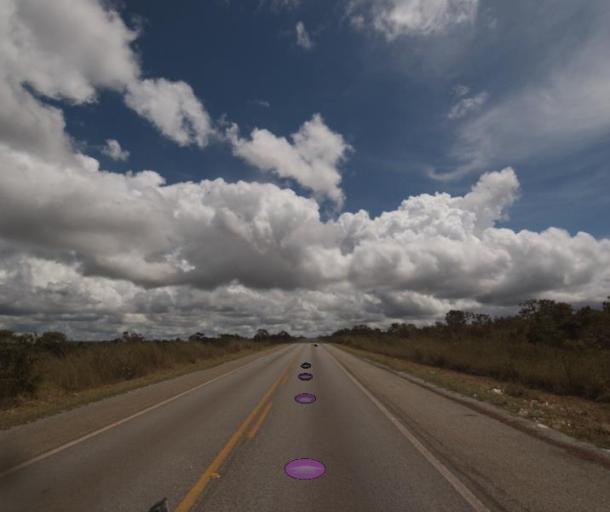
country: BR
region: Goias
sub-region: Pirenopolis
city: Pirenopolis
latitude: -15.7509
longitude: -48.6423
